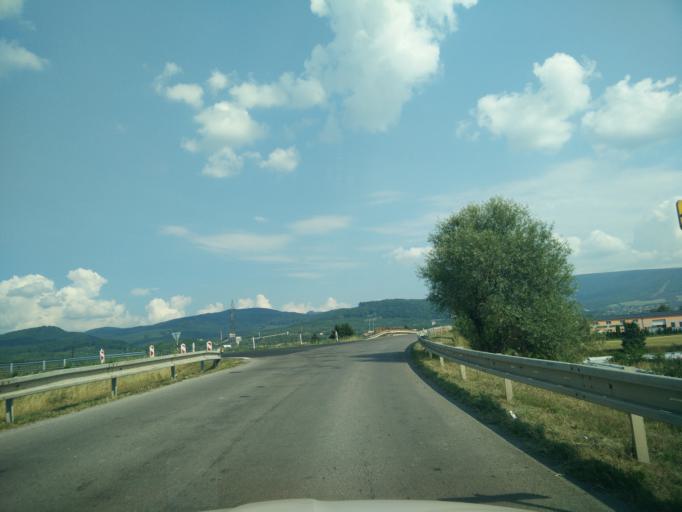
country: SK
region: Nitriansky
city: Prievidza
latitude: 48.7369
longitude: 18.6115
